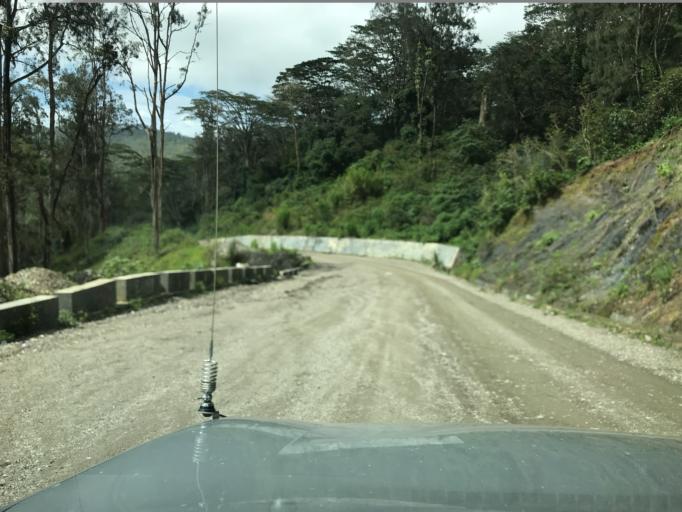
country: TL
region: Aileu
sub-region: Aileu Villa
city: Aileu
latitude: -8.6697
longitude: 125.5540
